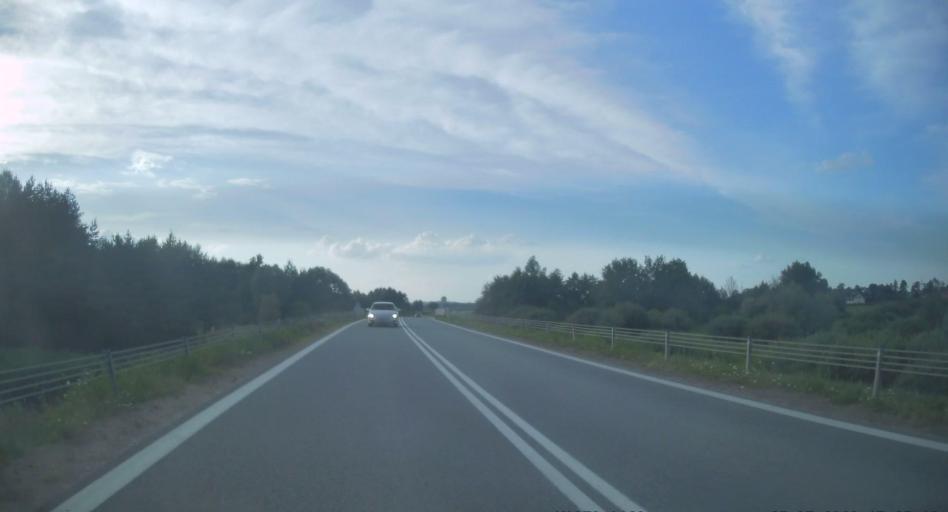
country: PL
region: Lesser Poland Voivodeship
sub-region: Powiat brzeski
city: Szczurowa
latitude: 50.0909
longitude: 20.6247
